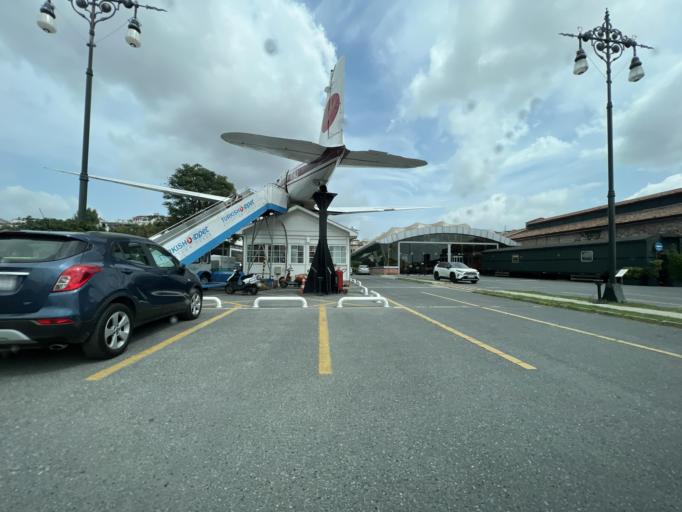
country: TR
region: Istanbul
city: Istanbul
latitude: 41.0416
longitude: 28.9484
